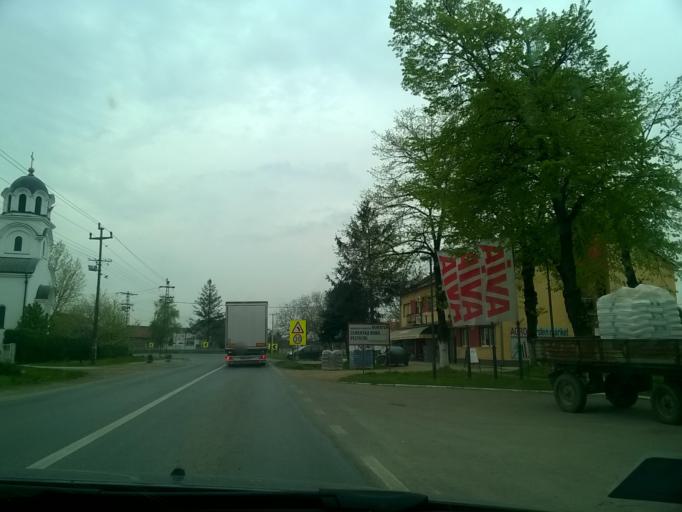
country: RS
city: Hrtkovci
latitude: 44.8818
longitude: 19.7631
